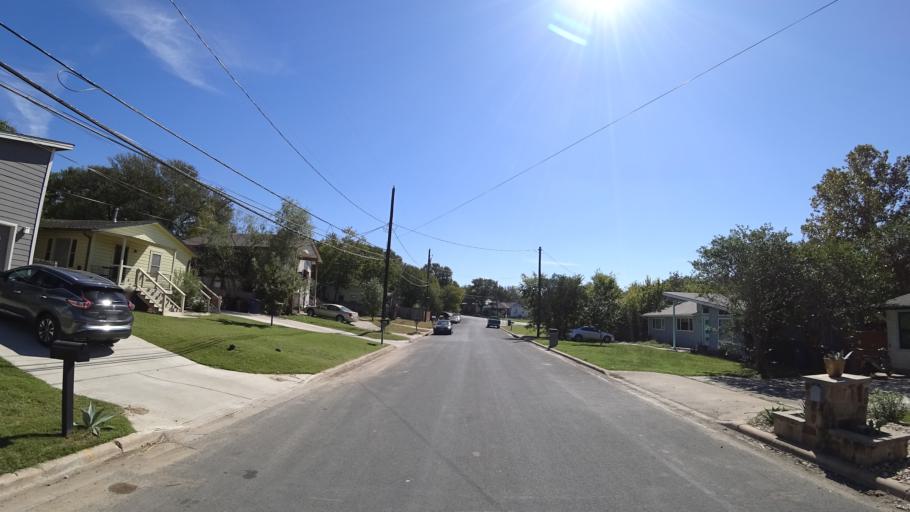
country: US
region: Texas
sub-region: Travis County
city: Austin
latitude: 30.2746
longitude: -97.6795
